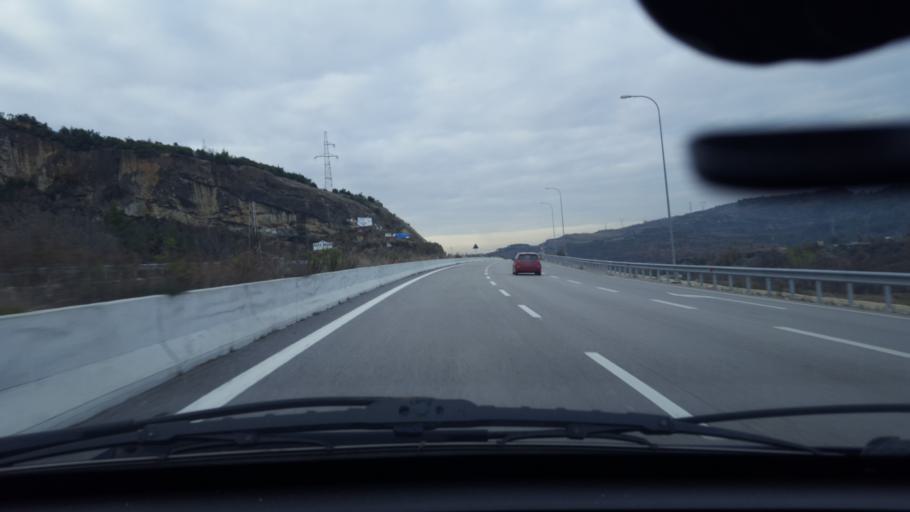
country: AL
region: Tirane
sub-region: Rrethi i Tiranes
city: Berzhite
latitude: 41.2286
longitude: 19.9307
